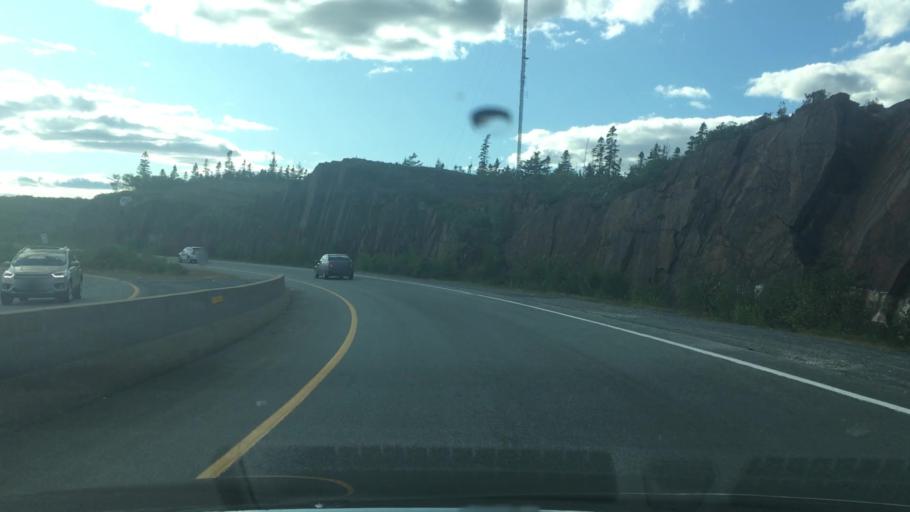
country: CA
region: Nova Scotia
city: Dartmouth
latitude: 44.6455
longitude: -63.6562
